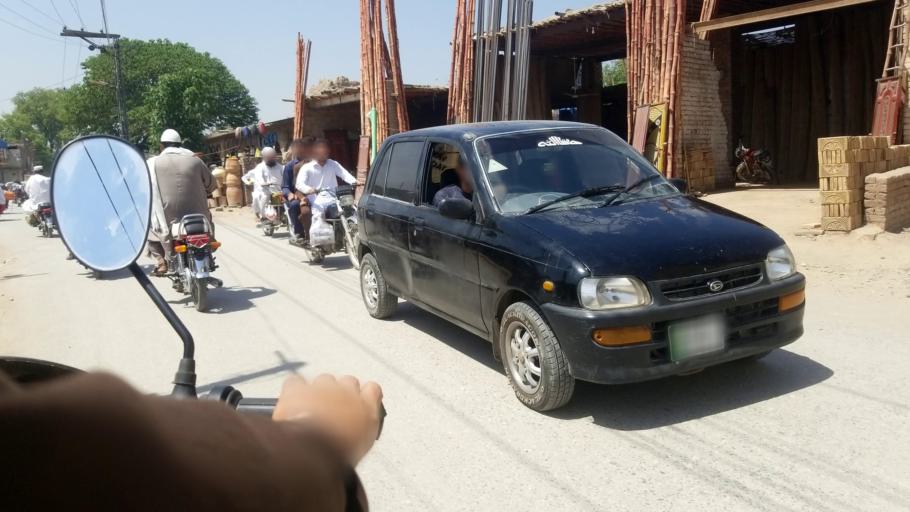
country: PK
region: Khyber Pakhtunkhwa
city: Peshawar
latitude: 34.0298
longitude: 71.4868
